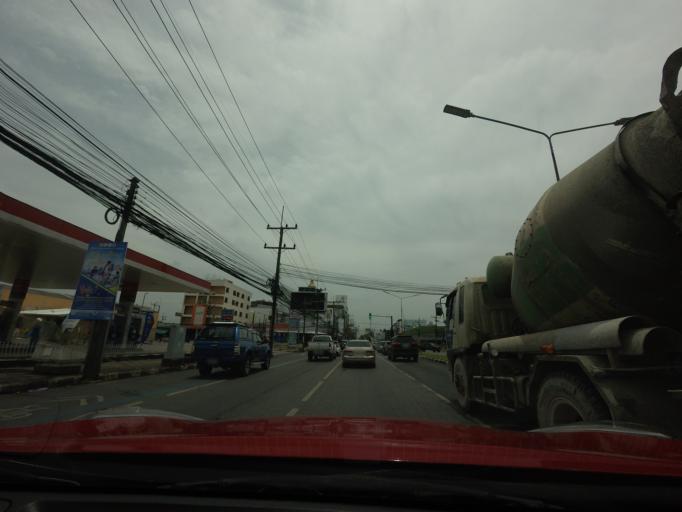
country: TH
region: Songkhla
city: Hat Yai
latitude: 6.9982
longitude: 100.4807
